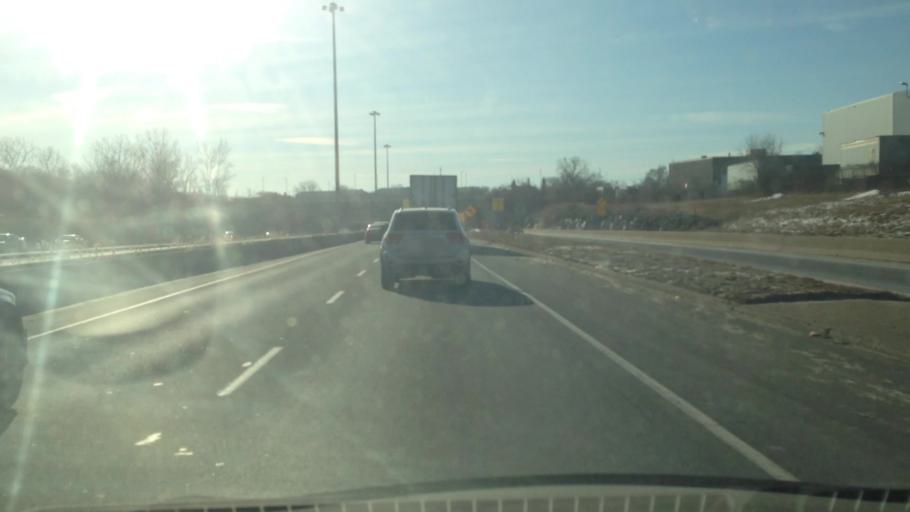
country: CA
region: Quebec
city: Cote-Saint-Luc
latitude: 45.4520
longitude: -73.6973
